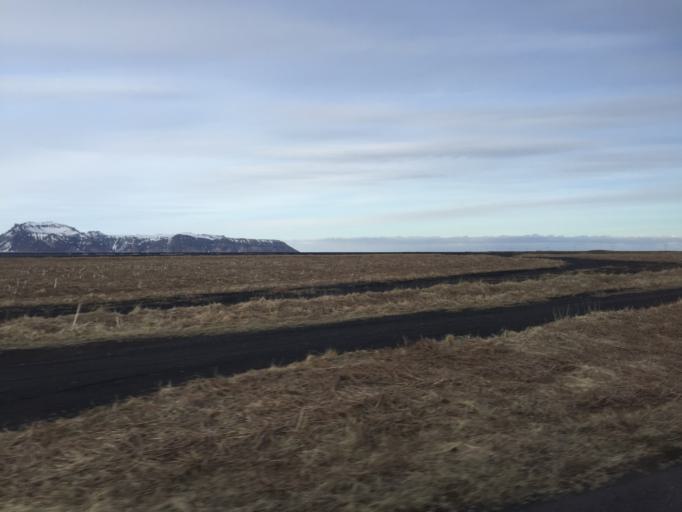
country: IS
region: South
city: Vestmannaeyjar
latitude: 63.4372
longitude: -18.8234
